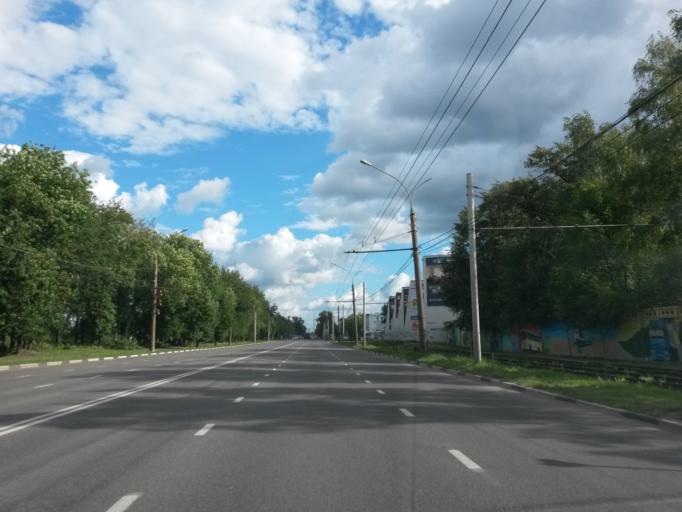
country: RU
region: Jaroslavl
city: Yaroslavl
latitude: 57.6512
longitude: 39.8470
